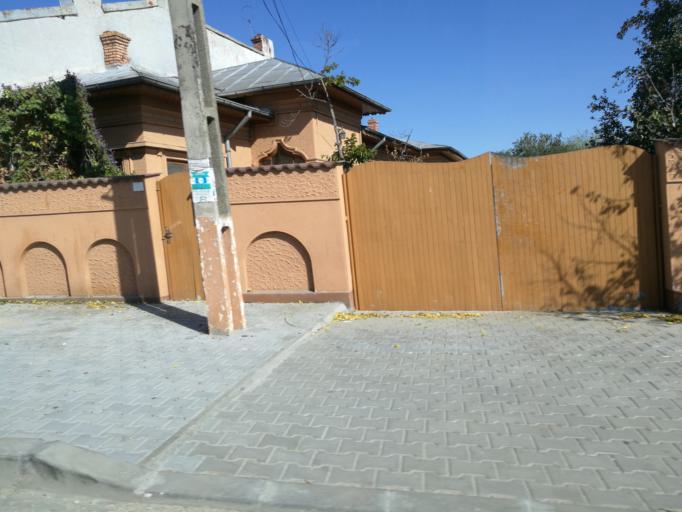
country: RO
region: Ilfov
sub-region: Comuna Dragomiresti-Vale
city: Dragomiresti-Deal
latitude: 44.4596
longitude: 25.9463
